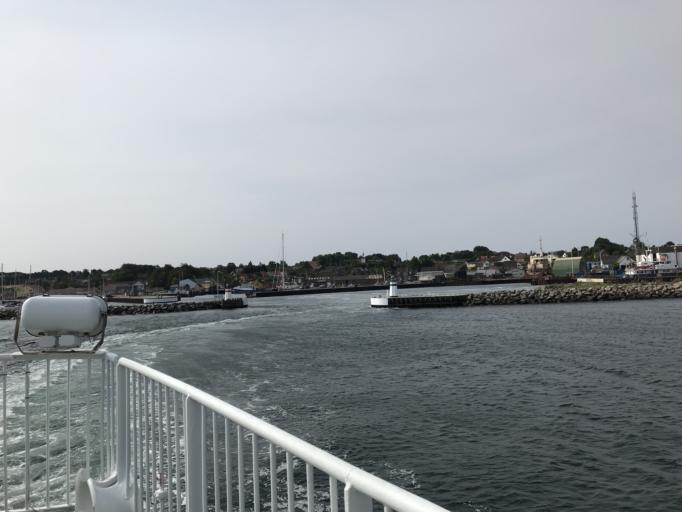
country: DK
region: South Denmark
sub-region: Faaborg-Midtfyn Kommune
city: Faaborg
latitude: 54.9447
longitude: 10.2589
